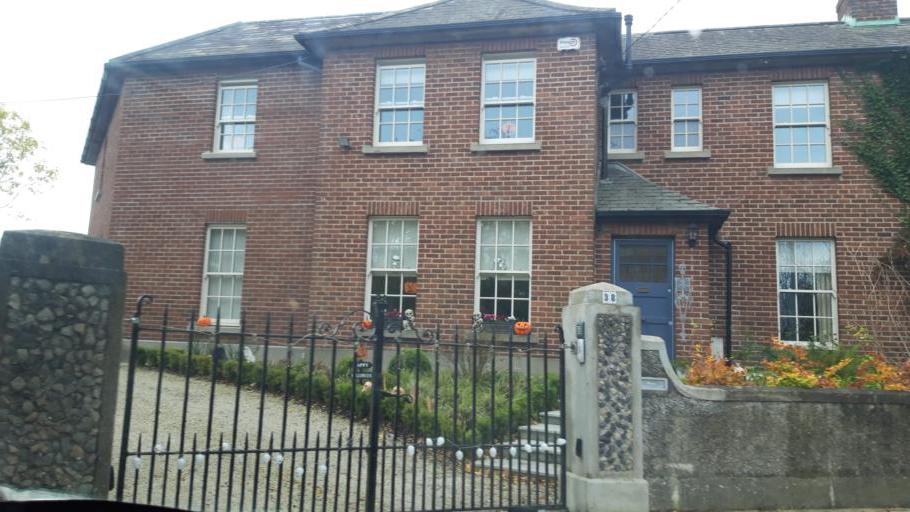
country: IE
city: Milltown
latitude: 53.3103
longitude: -6.2412
